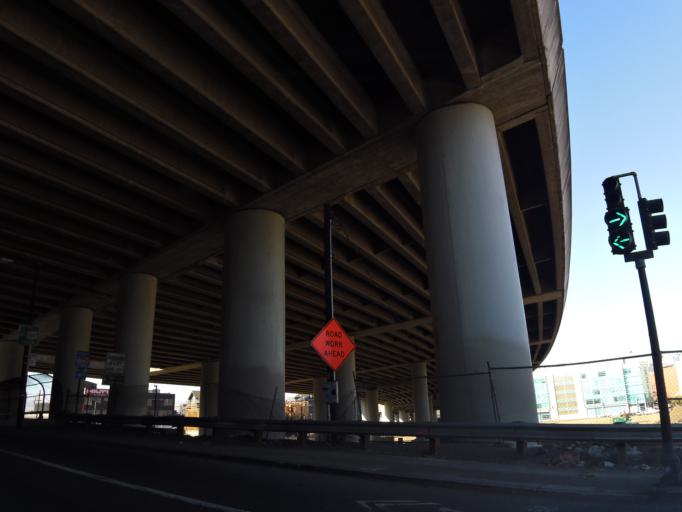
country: US
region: California
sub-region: San Francisco County
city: San Francisco
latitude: 37.7642
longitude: -122.3924
